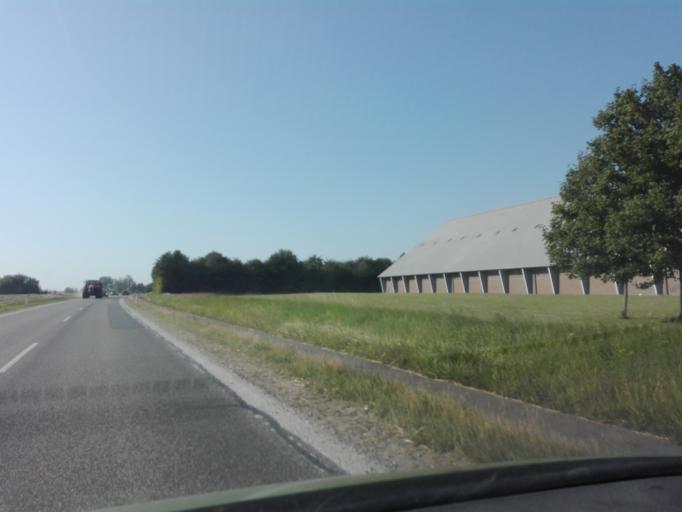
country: DK
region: Central Jutland
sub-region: Odder Kommune
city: Odder
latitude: 55.9368
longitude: 10.2188
